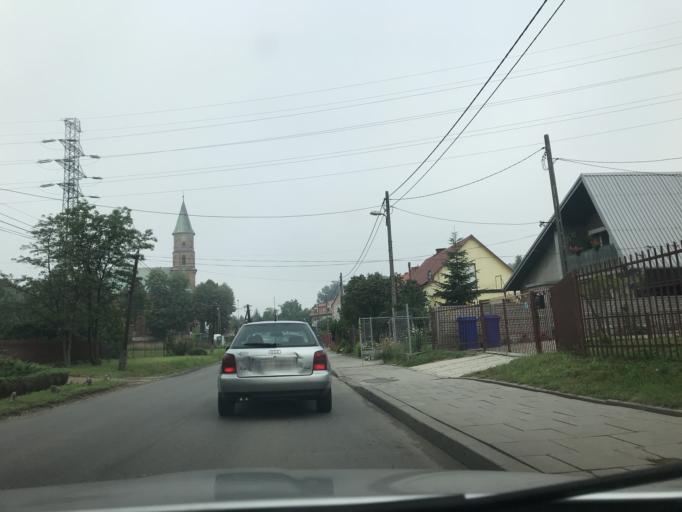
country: PL
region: Lesser Poland Voivodeship
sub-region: Powiat krakowski
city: Ochojno
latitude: 50.0056
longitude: 19.9847
